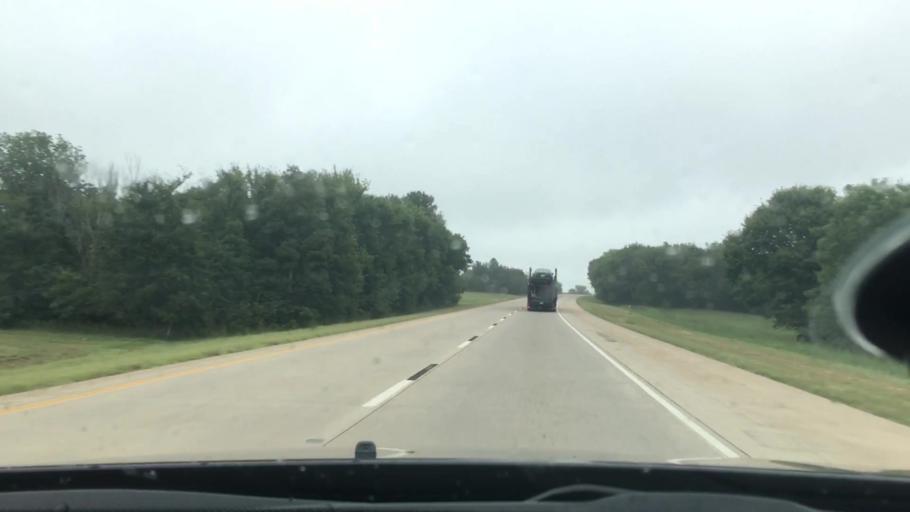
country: US
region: Oklahoma
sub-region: Okmulgee County
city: Henryetta
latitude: 35.4327
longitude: -95.9366
